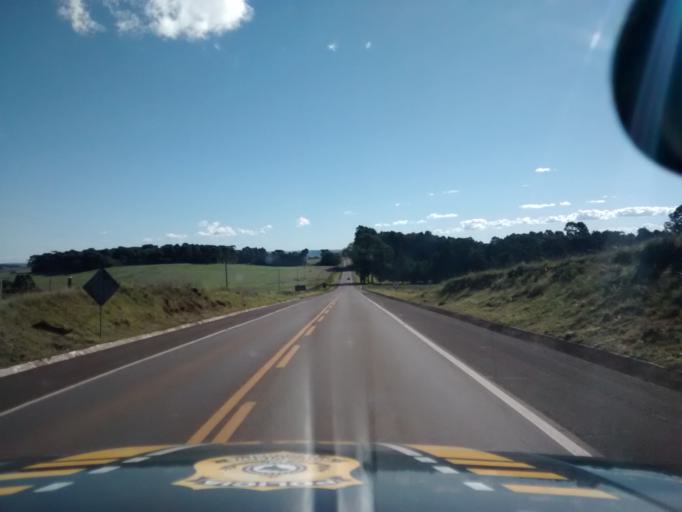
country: BR
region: Rio Grande do Sul
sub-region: Lagoa Vermelha
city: Lagoa Vermelha
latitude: -28.3226
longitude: -51.2340
